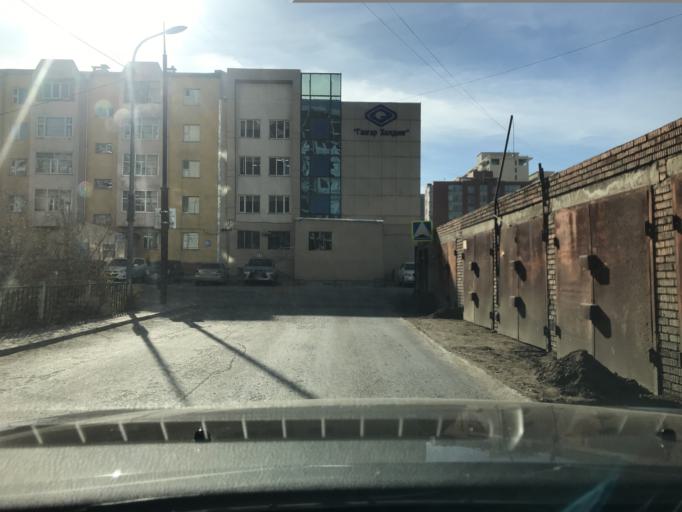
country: MN
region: Ulaanbaatar
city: Ulaanbaatar
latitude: 47.9117
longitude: 106.9401
